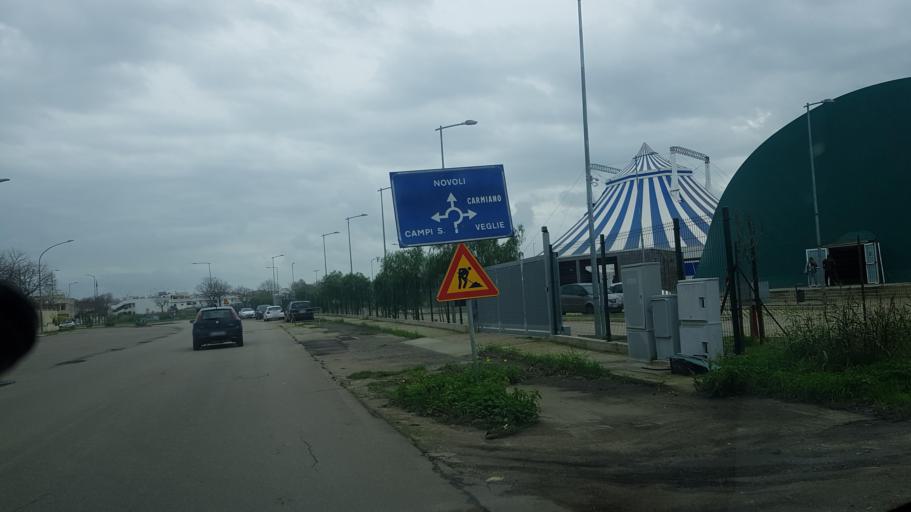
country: IT
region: Apulia
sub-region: Provincia di Lecce
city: Novoli
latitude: 40.3785
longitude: 18.0413
